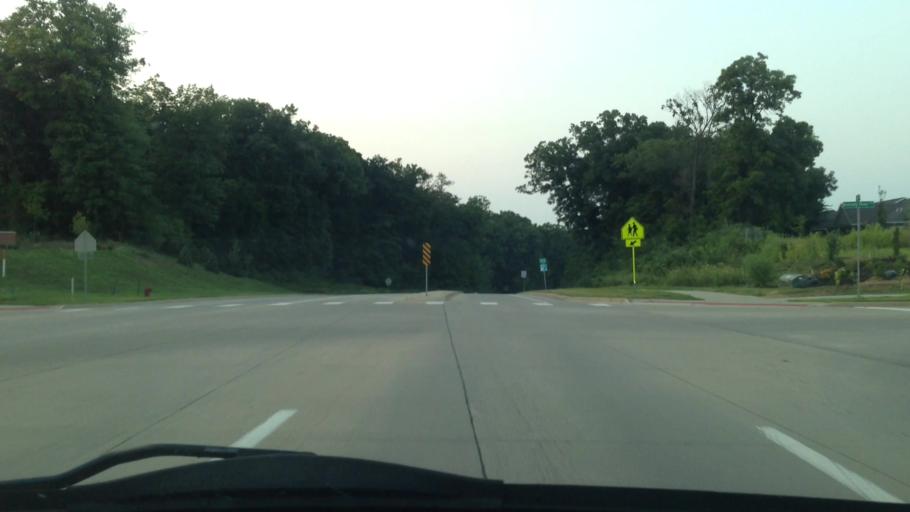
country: US
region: Iowa
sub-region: Johnson County
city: Coralville
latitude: 41.6690
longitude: -91.6036
